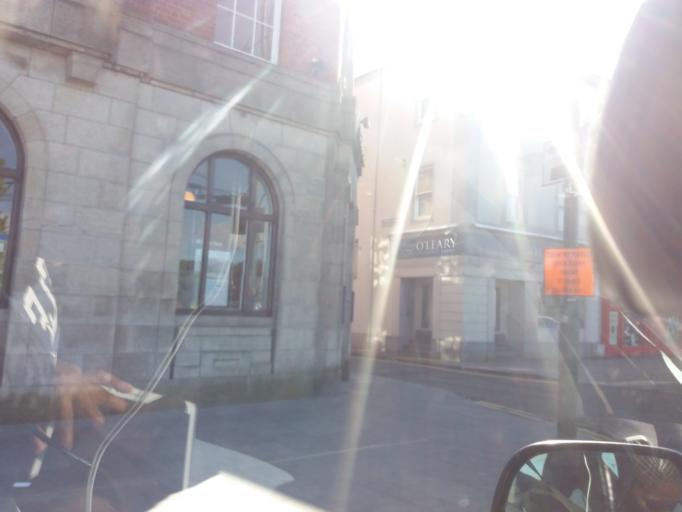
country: IE
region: Munster
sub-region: Waterford
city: Waterford
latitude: 52.2614
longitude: -7.1091
